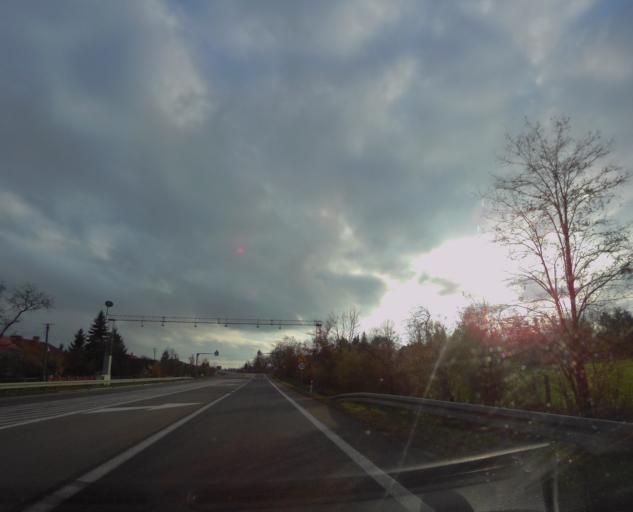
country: PL
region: Subcarpathian Voivodeship
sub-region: Powiat przemyski
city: Orly
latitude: 49.9013
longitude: 22.8168
